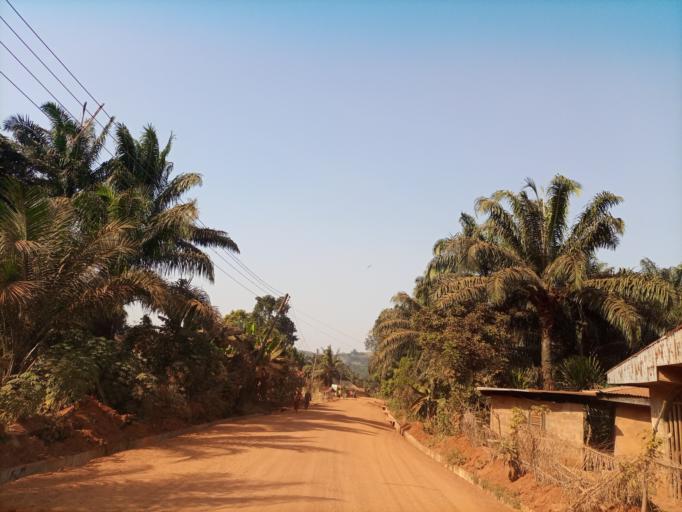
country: NG
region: Enugu
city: Aku
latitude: 6.6965
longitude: 7.3264
